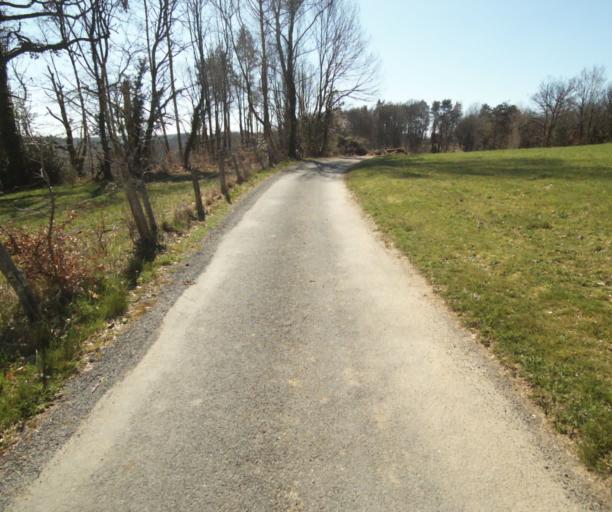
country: FR
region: Limousin
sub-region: Departement de la Correze
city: Saint-Mexant
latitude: 45.3050
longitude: 1.6392
